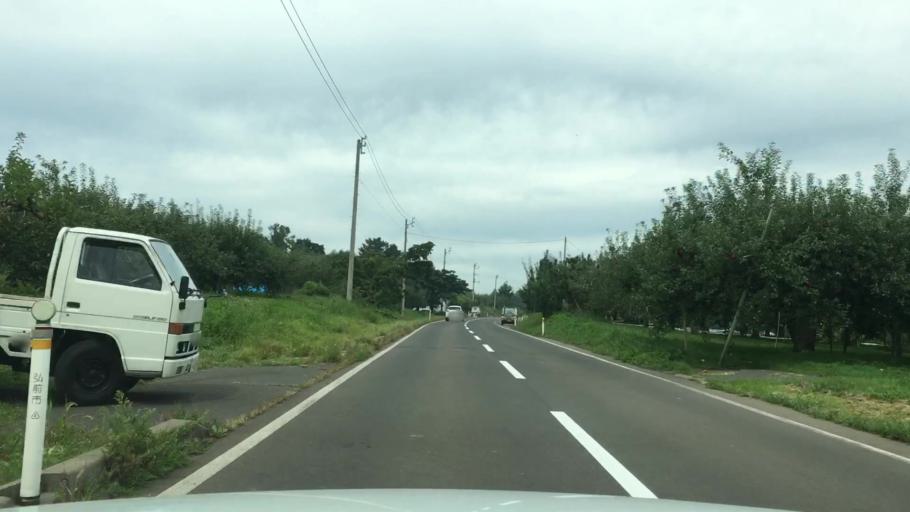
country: JP
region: Aomori
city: Hirosaki
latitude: 40.6710
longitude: 140.3870
